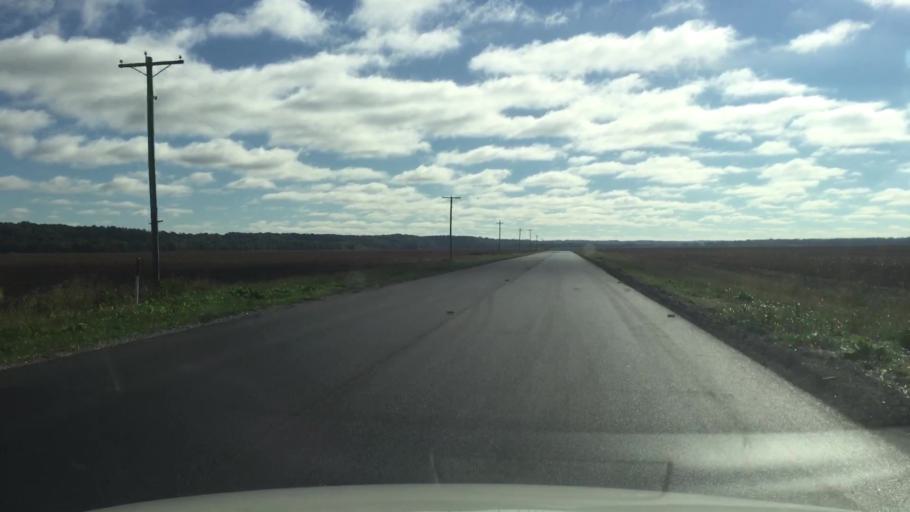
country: US
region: Missouri
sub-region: Howard County
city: New Franklin
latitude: 38.9956
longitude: -92.6615
